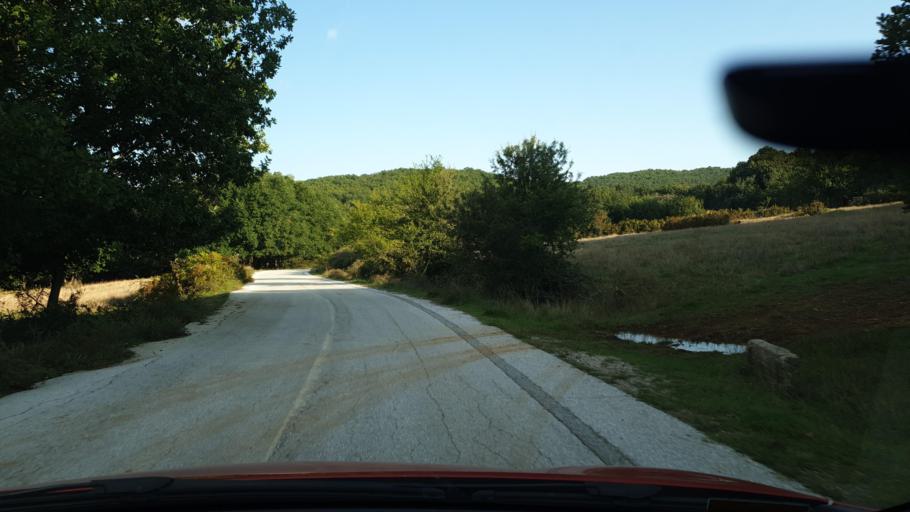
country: GR
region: Central Macedonia
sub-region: Nomos Chalkidikis
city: Galatista
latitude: 40.5058
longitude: 23.2248
